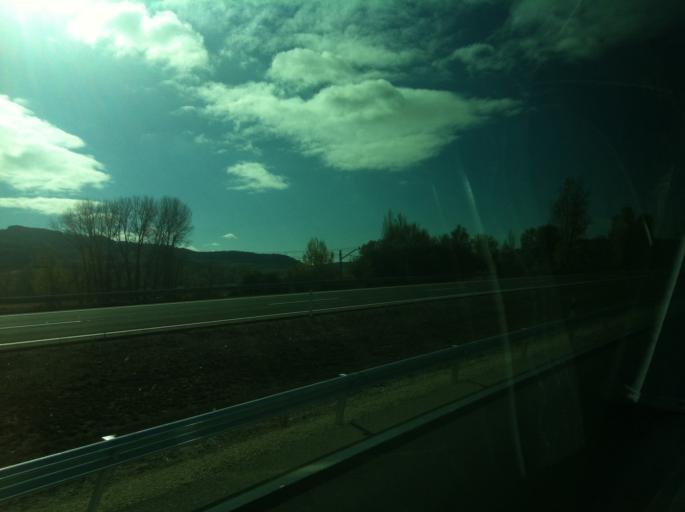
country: ES
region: Castille and Leon
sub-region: Provincia de Burgos
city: Santa Olalla de Bureba
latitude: 42.4756
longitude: -3.4360
